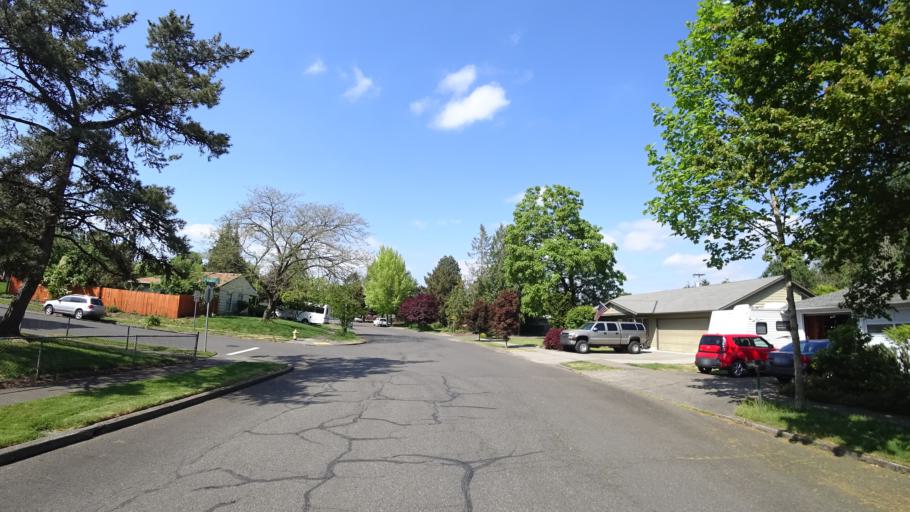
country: US
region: Oregon
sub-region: Washington County
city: Beaverton
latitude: 45.4661
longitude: -122.7915
